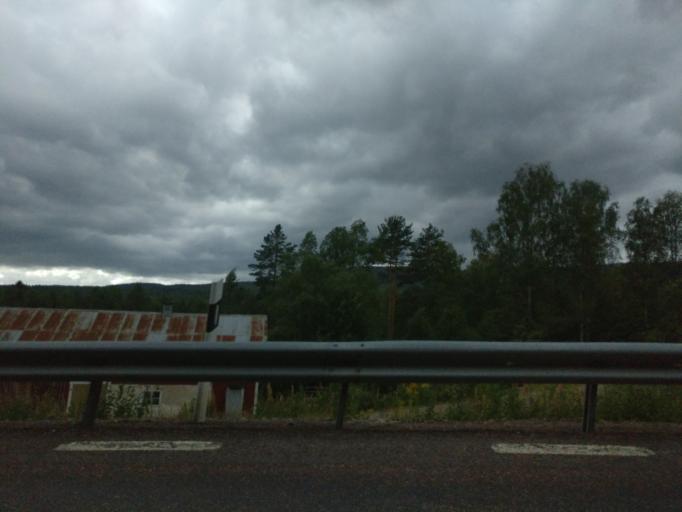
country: SE
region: Vaermland
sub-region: Torsby Kommun
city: Torsby
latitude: 60.5997
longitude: 13.0657
